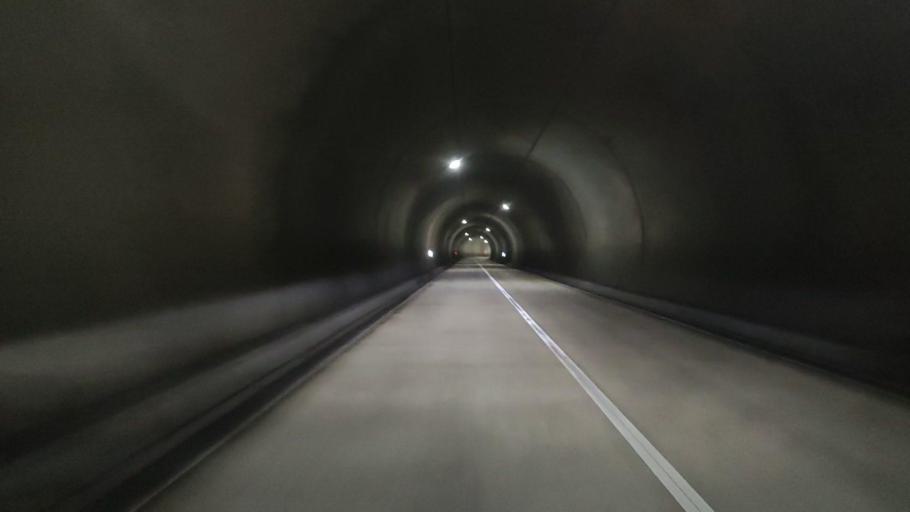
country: JP
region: Wakayama
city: Shingu
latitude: 33.8763
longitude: 135.8585
